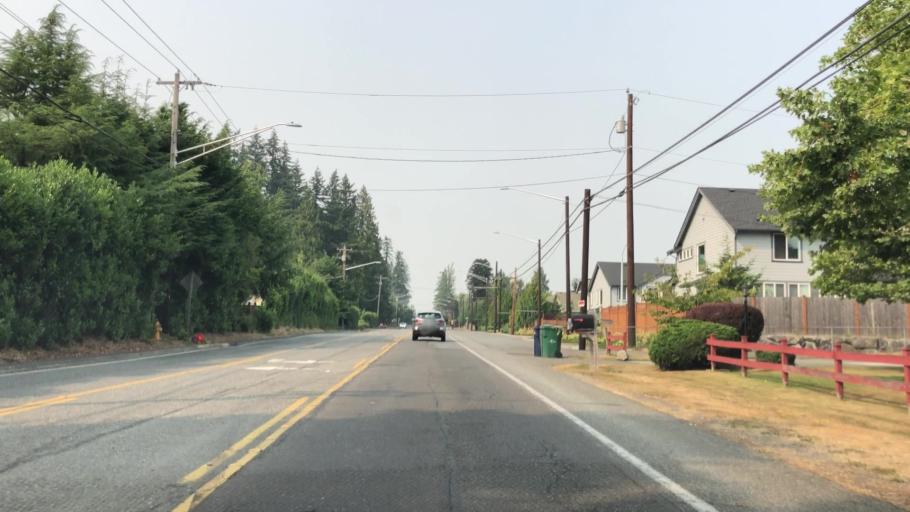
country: US
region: Washington
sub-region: Snohomish County
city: Alderwood Manor
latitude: 47.8433
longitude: -122.2818
